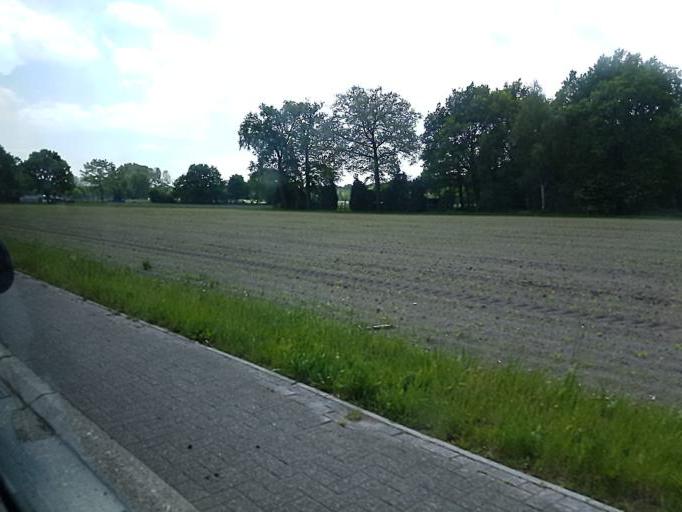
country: BE
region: Flanders
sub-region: Provincie Limburg
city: Neerpelt
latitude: 51.2091
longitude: 5.4990
